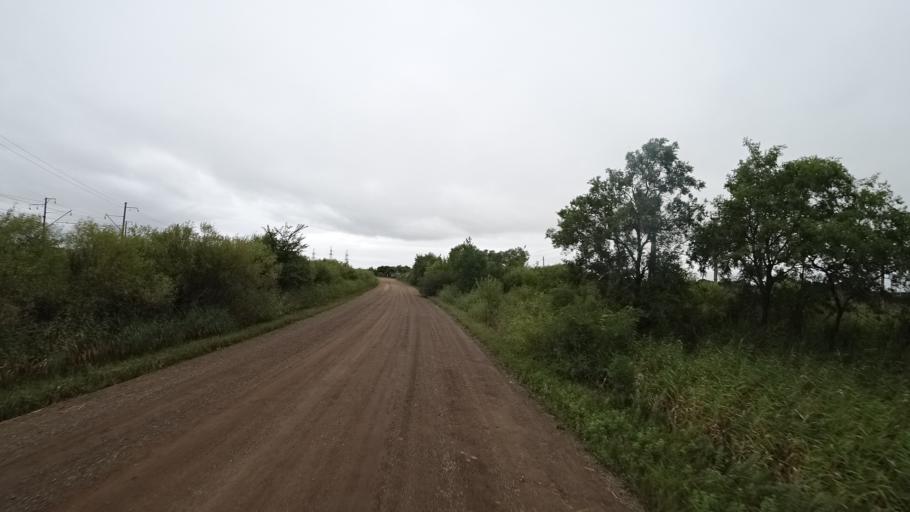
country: RU
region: Primorskiy
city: Chernigovka
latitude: 44.3350
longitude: 132.5250
